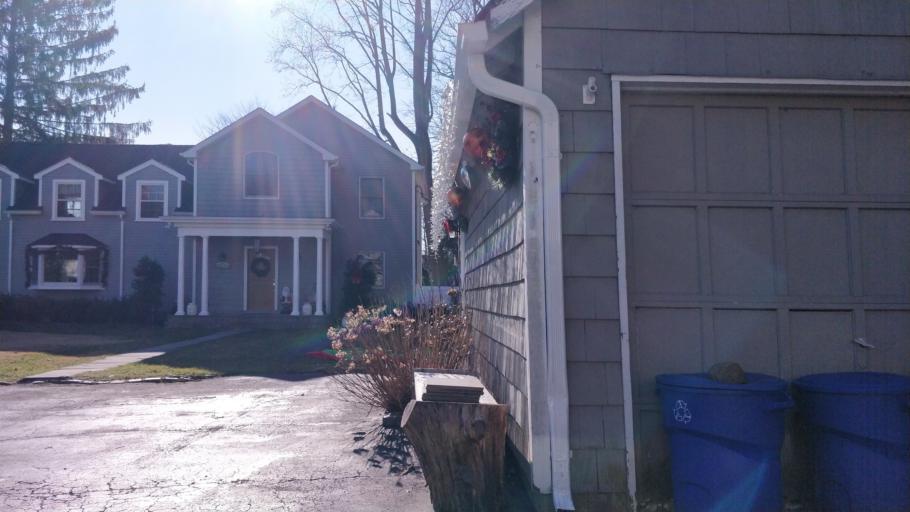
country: US
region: New York
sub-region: Nassau County
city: Glen Head
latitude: 40.8403
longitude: -73.6244
